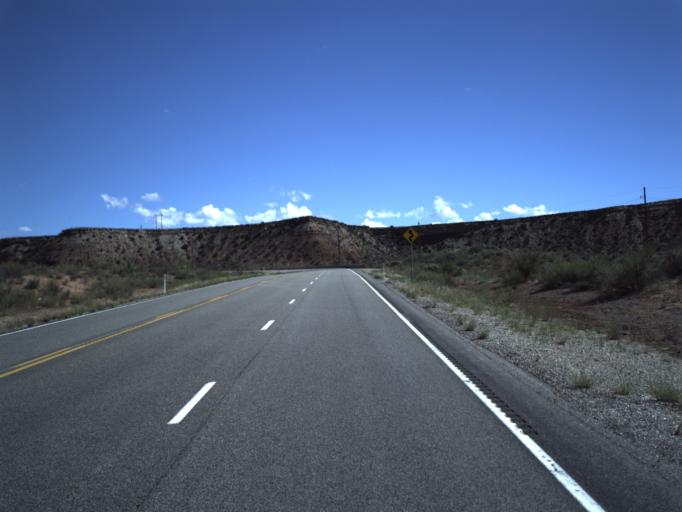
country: US
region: Utah
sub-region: Washington County
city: Hurricane
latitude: 37.1445
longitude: -113.2540
